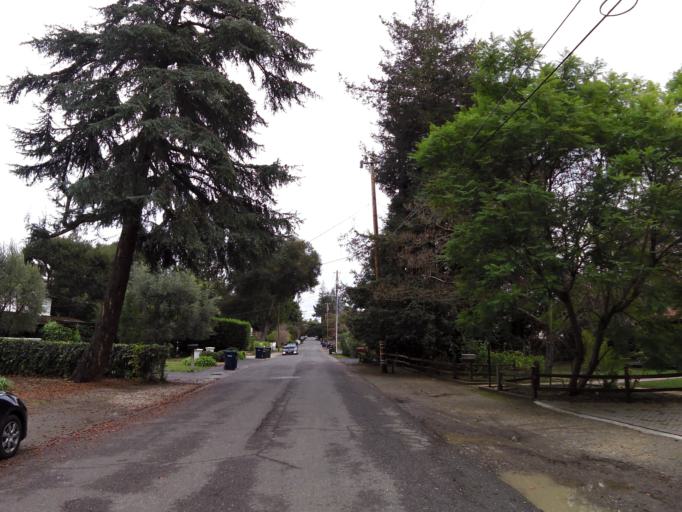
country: US
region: California
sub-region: Santa Clara County
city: Loyola
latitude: 37.3576
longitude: -122.0917
